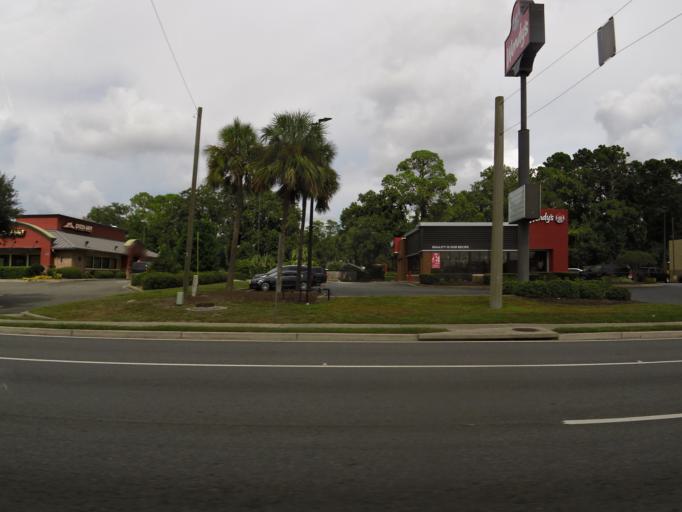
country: US
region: Georgia
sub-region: Glynn County
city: Dock Junction
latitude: 31.2167
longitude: -81.5184
